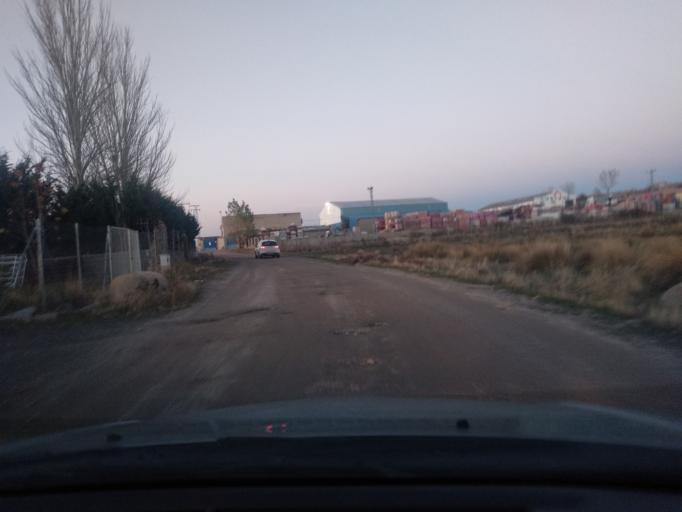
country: ES
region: Castille and Leon
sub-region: Provincia de Segovia
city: San Cristobal de Segovia
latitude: 40.9706
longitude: -4.0828
